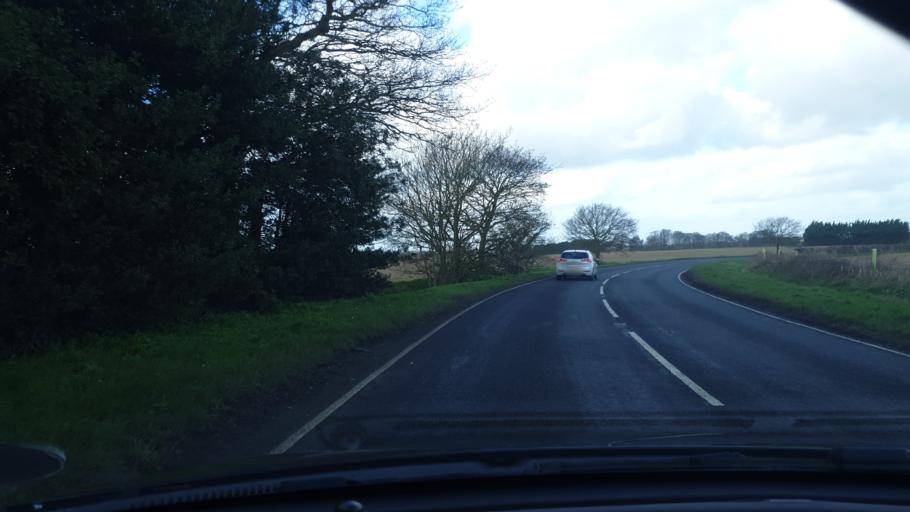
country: GB
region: England
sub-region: Essex
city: Mistley
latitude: 51.9076
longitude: 1.0820
